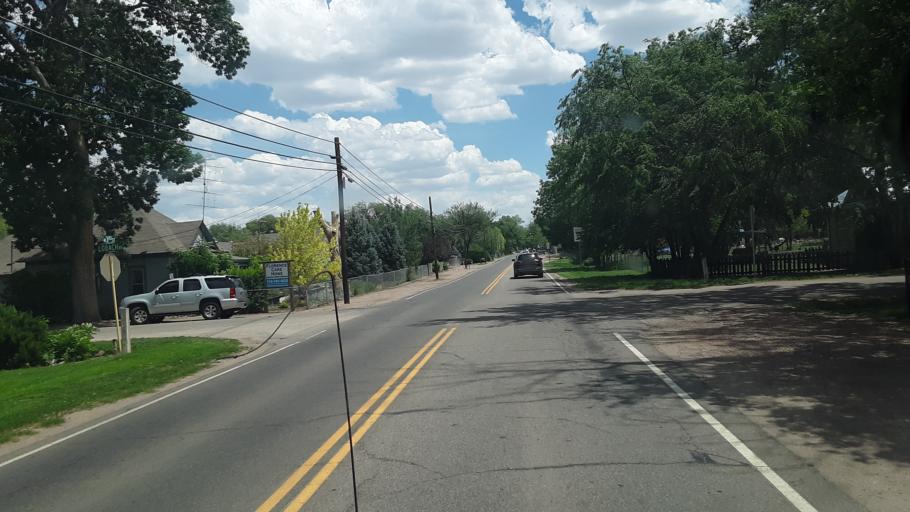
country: US
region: Colorado
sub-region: Fremont County
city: Florence
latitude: 38.3988
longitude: -105.1318
